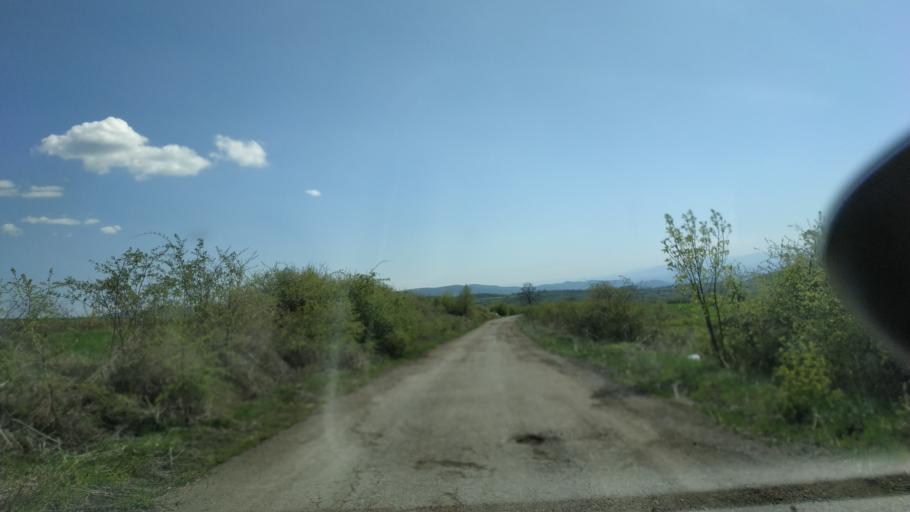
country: RS
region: Central Serbia
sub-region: Zajecarski Okrug
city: Soko Banja
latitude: 43.5249
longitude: 21.9060
